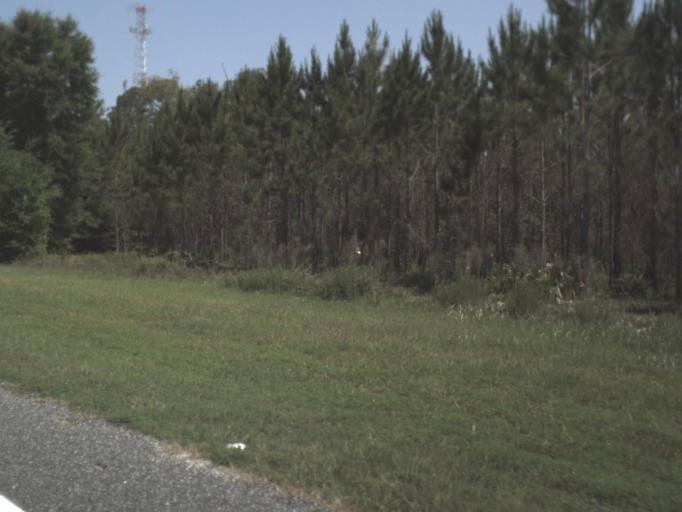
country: US
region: Florida
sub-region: Clay County
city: Middleburg
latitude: 29.9801
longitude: -81.9304
